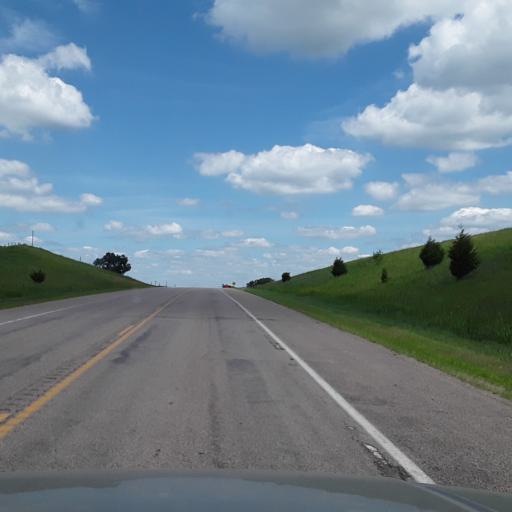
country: US
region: Nebraska
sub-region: Nance County
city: Genoa
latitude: 41.4724
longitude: -97.7019
